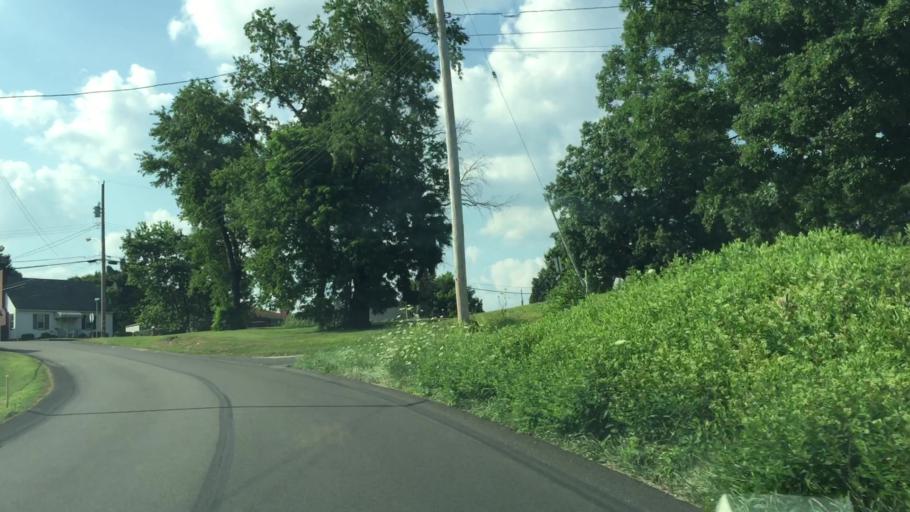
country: US
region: Pennsylvania
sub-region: Allegheny County
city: Coraopolis
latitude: 40.5103
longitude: -80.1718
